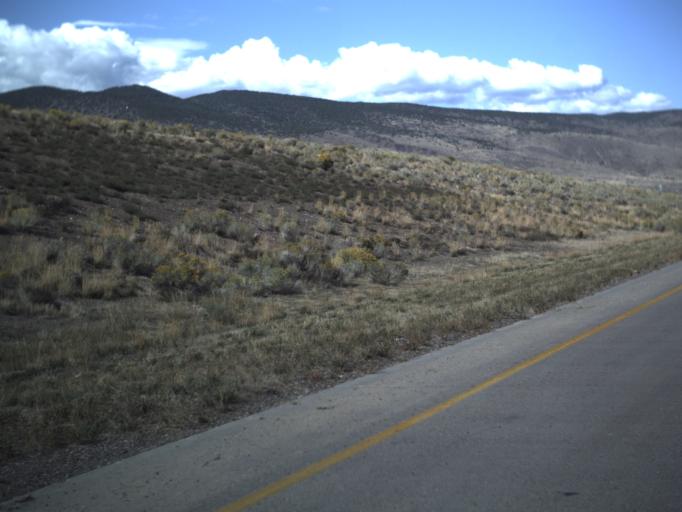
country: US
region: Utah
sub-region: Sevier County
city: Monroe
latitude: 38.6250
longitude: -112.2253
